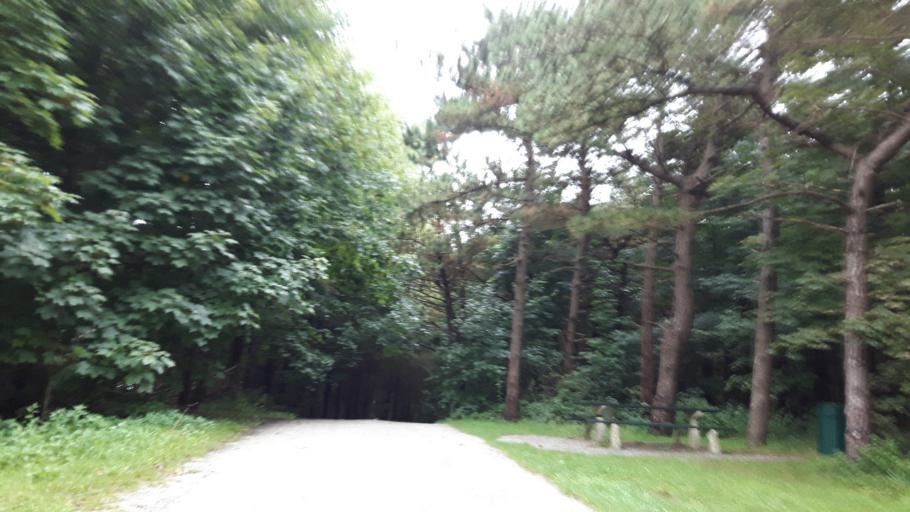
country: NL
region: Friesland
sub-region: Gemeente Ameland
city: Nes
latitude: 53.4532
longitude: 5.7568
